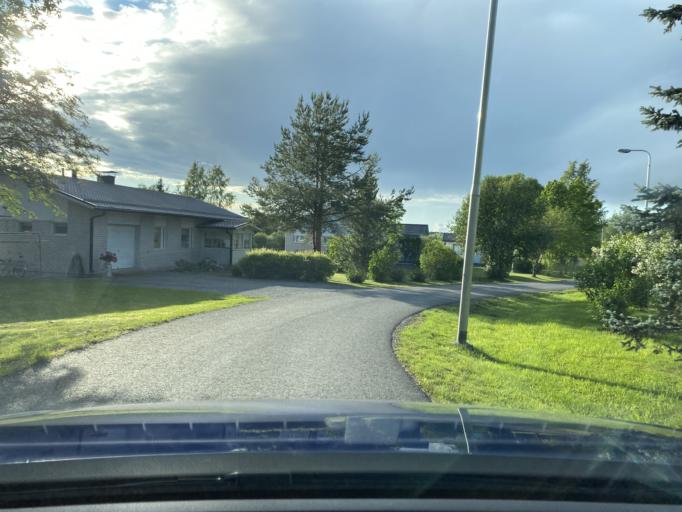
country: FI
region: Pirkanmaa
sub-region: Lounais-Pirkanmaa
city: Punkalaidun
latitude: 61.1166
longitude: 23.1160
